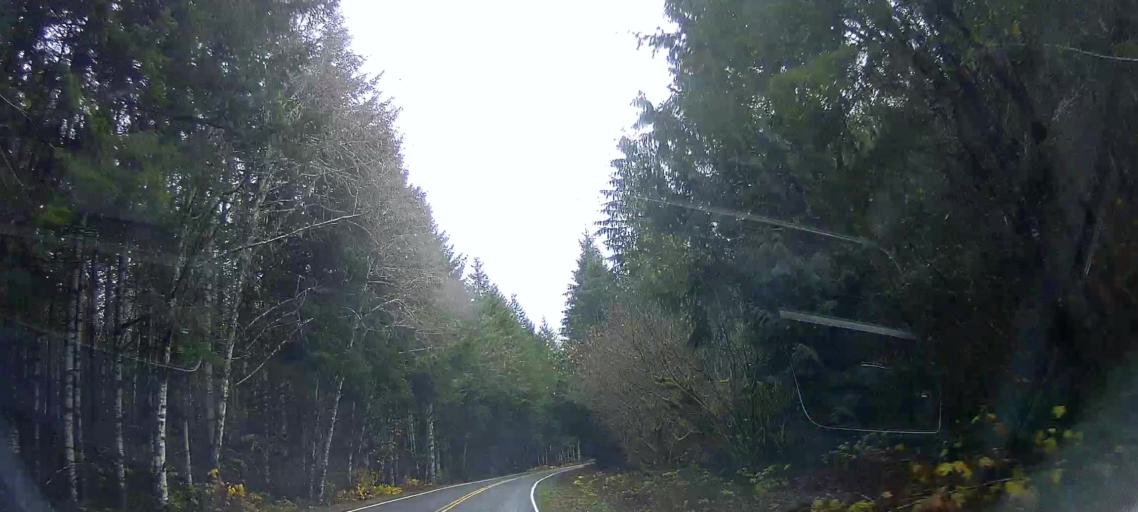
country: US
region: Washington
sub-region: Snohomish County
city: Darrington
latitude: 48.4849
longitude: -121.4928
